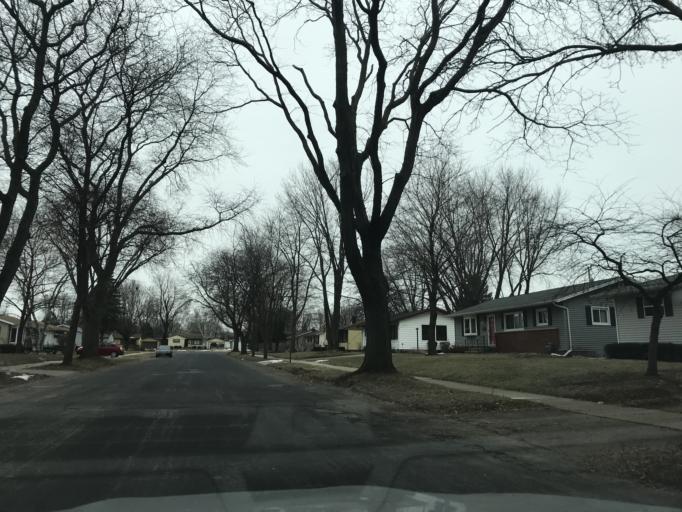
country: US
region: Wisconsin
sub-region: Dane County
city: Monona
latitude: 43.0951
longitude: -89.3034
